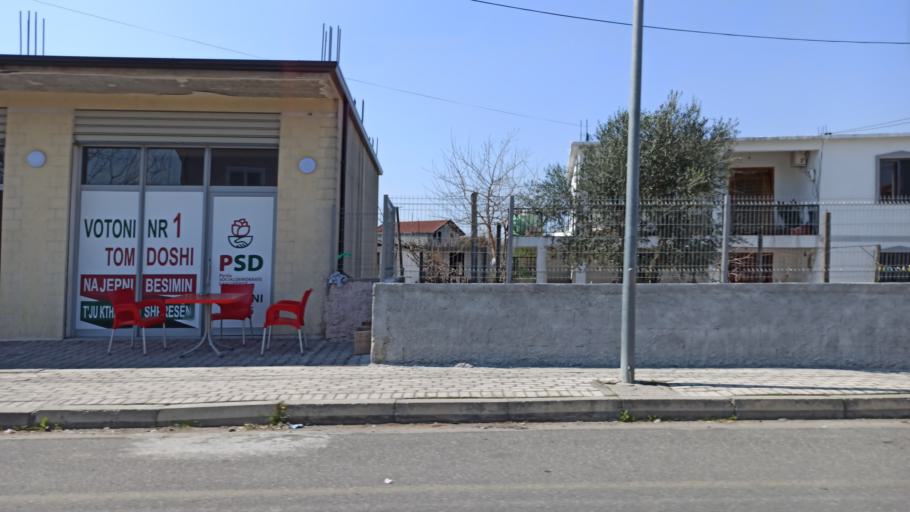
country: AL
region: Shkoder
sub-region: Rrethi i Shkodres
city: Shkoder
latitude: 42.0576
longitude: 19.5246
